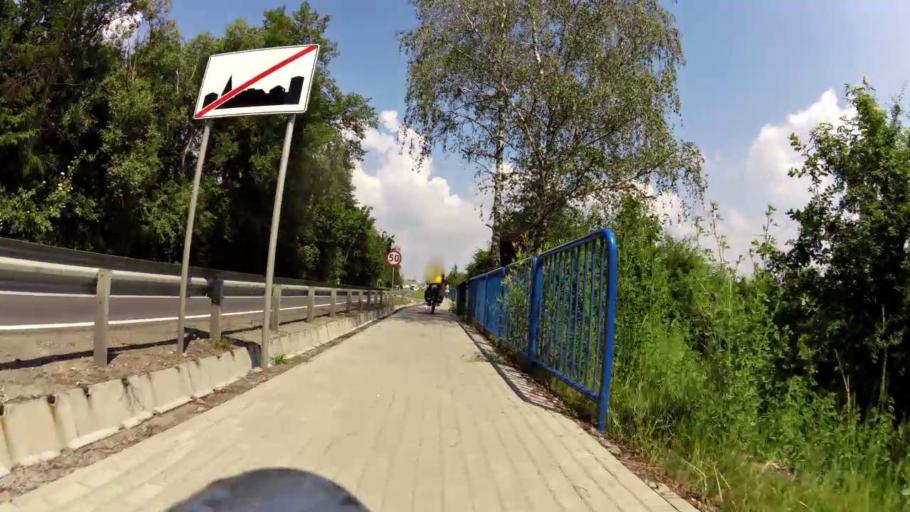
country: PL
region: Kujawsko-Pomorskie
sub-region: Powiat bydgoski
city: Koronowo
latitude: 53.2854
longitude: 17.9322
